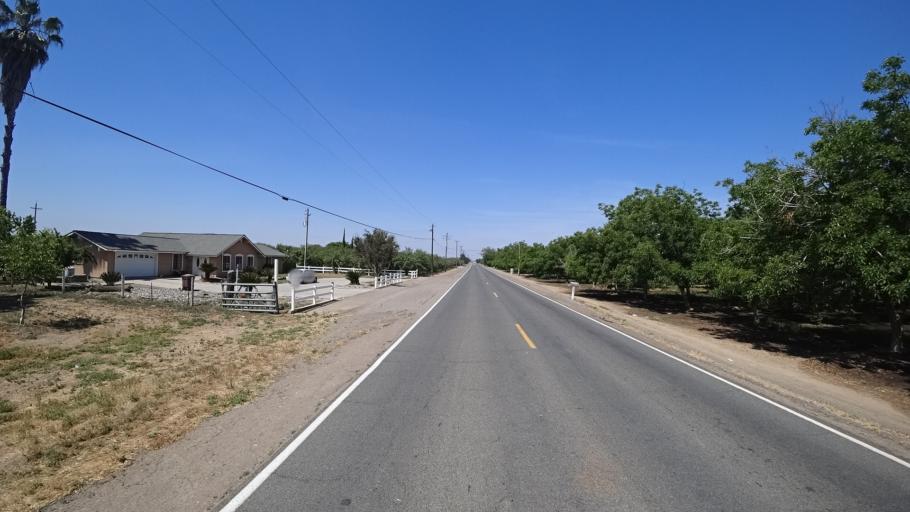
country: US
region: California
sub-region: Fresno County
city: Riverdale
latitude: 36.4020
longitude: -119.7731
